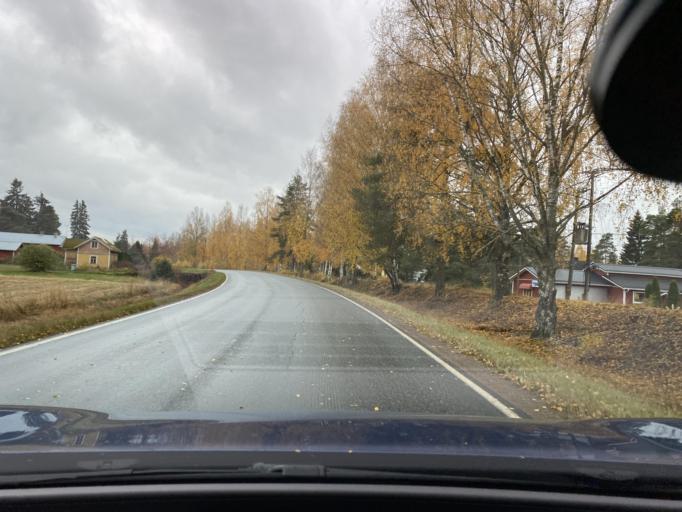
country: FI
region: Satakunta
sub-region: Pori
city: Kokemaeki
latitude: 61.2647
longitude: 22.4016
